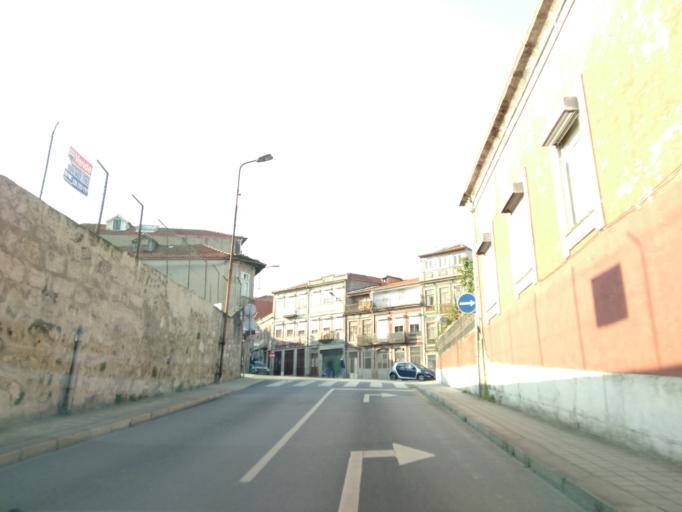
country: PT
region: Porto
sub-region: Vila Nova de Gaia
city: Oliveira do Douro
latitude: 41.1471
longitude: -8.5867
